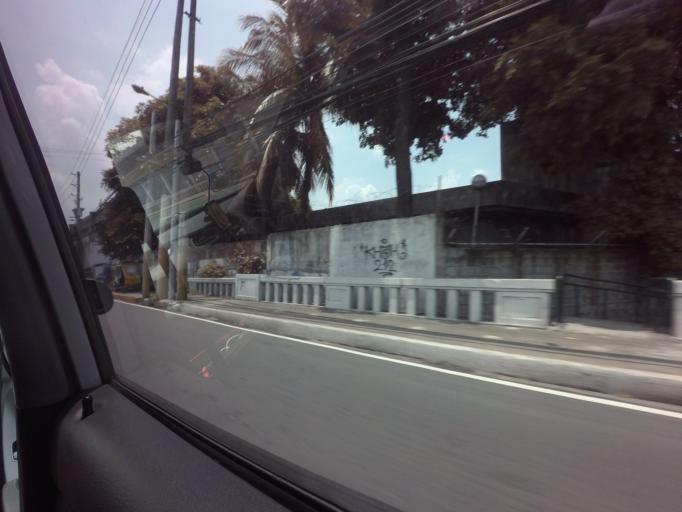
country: PH
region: Metro Manila
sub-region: City of Manila
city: Quiapo
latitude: 14.5944
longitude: 120.9883
